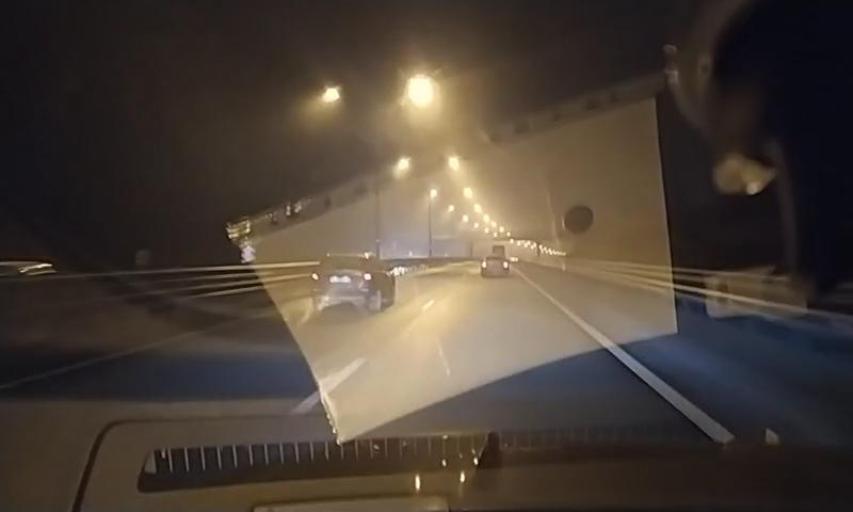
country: RU
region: Leningrad
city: Bugry
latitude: 60.1189
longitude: 30.3858
